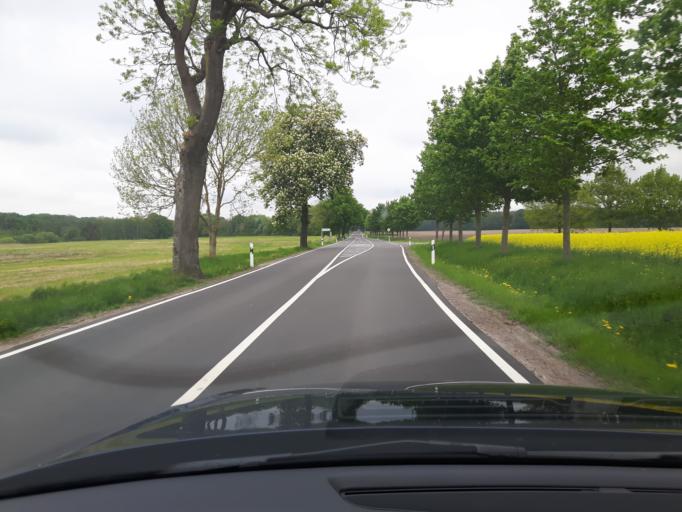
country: DE
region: Mecklenburg-Vorpommern
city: Gnoien
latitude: 53.9893
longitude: 12.6862
